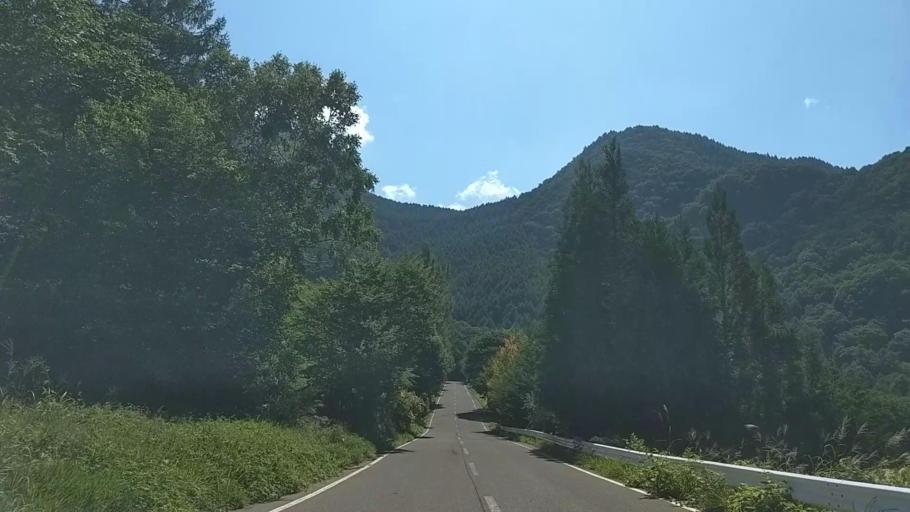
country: JP
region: Nagano
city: Matsumoto
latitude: 36.2077
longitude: 138.0929
